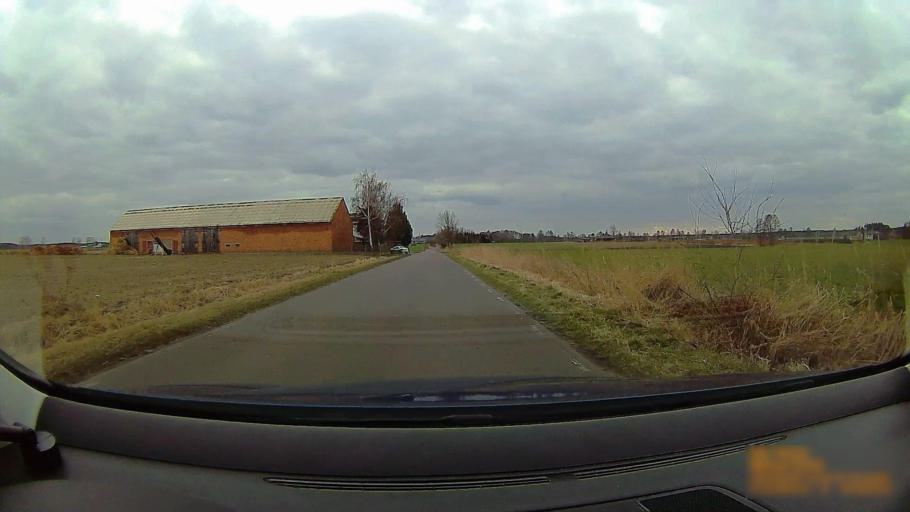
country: PL
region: Greater Poland Voivodeship
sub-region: Powiat koninski
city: Rzgow Pierwszy
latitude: 52.1401
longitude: 18.0564
